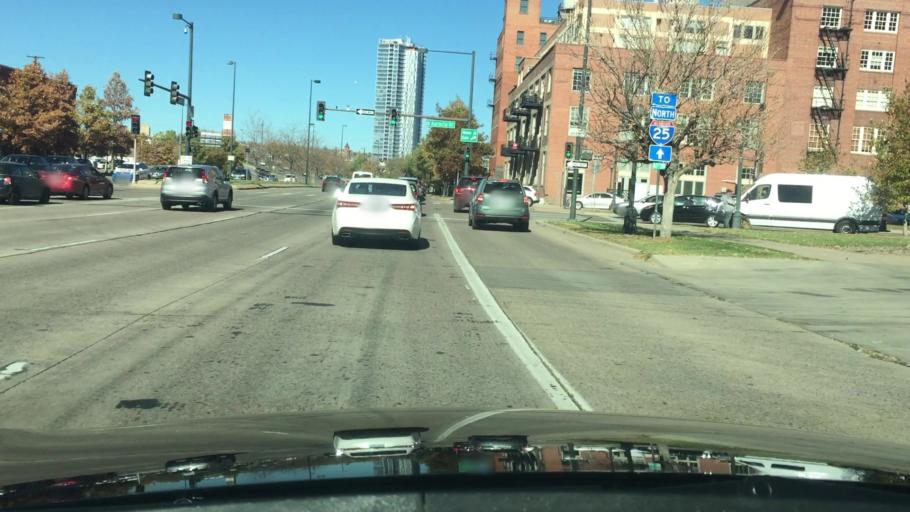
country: US
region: Colorado
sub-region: Denver County
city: Denver
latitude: 39.7482
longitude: -105.0028
